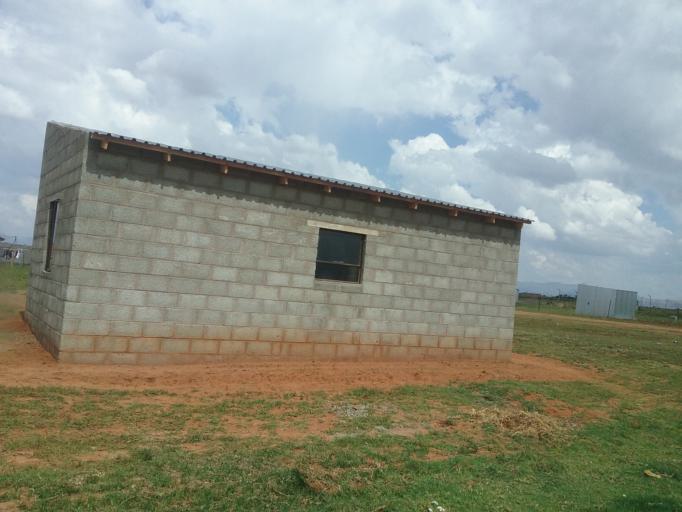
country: LS
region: Maseru
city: Maseru
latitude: -29.4208
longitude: 27.5652
